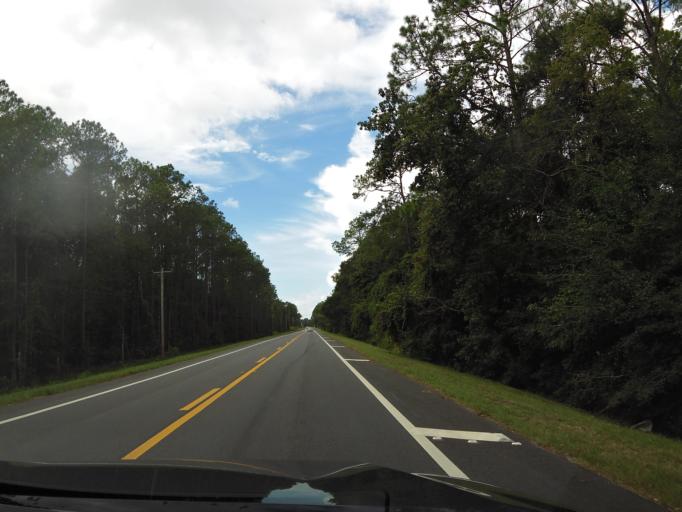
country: US
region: Florida
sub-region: Clay County
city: Middleburg
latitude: 30.1128
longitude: -81.9793
